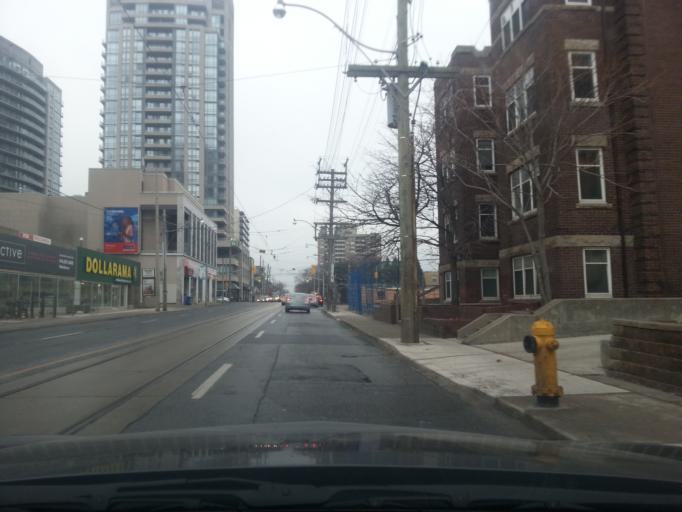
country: CA
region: Ontario
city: Toronto
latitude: 43.6821
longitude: -79.4178
